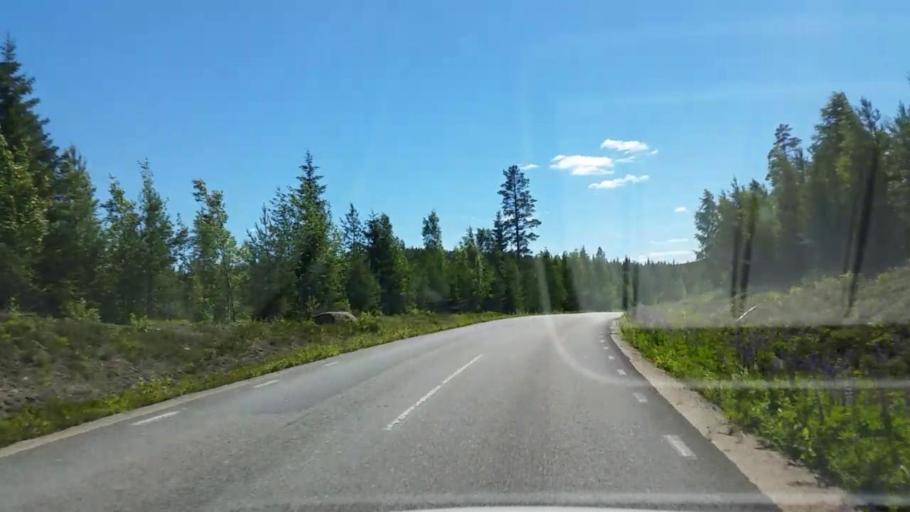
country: SE
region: Gaevleborg
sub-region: Ljusdals Kommun
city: Farila
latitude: 61.6457
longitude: 15.5928
